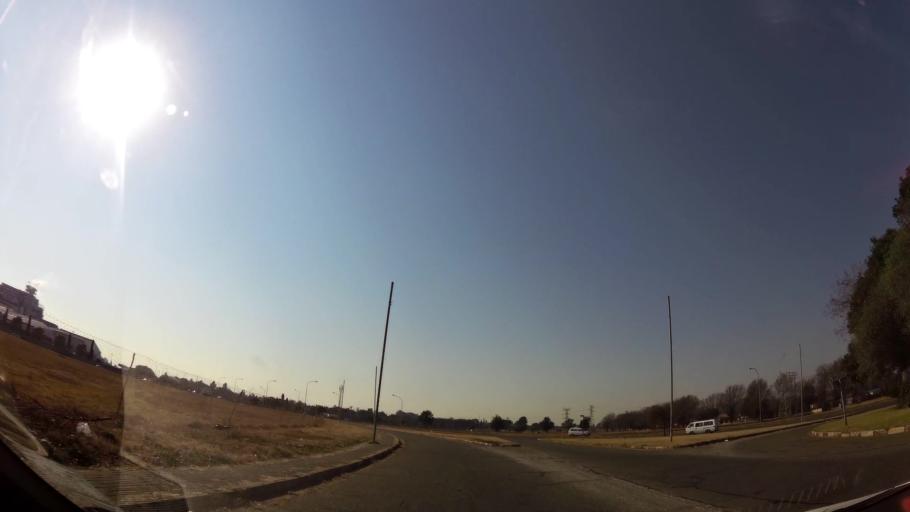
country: ZA
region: Gauteng
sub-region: Ekurhuleni Metropolitan Municipality
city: Boksburg
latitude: -26.2237
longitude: 28.2683
